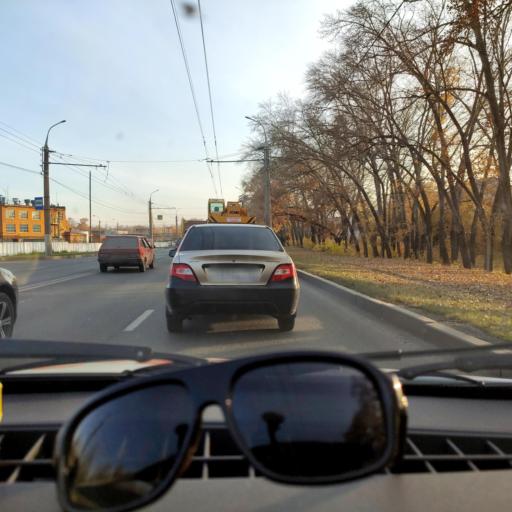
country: RU
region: Bashkortostan
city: Sterlitamak
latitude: 53.6688
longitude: 55.9494
